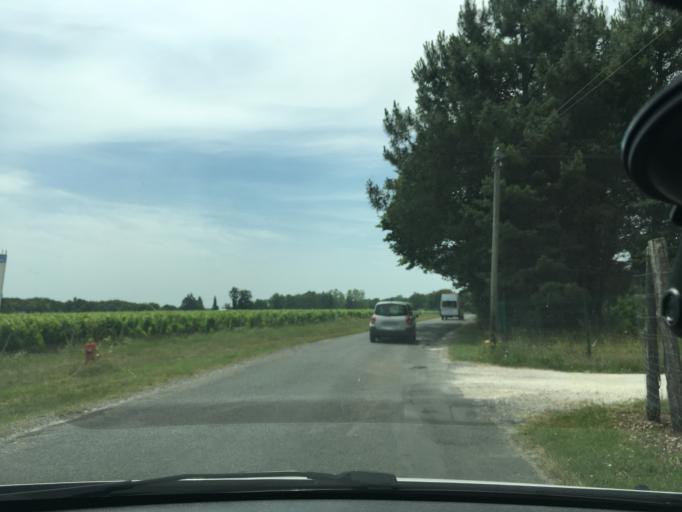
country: FR
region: Aquitaine
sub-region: Departement de la Gironde
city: Castelnau-de-Medoc
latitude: 45.0411
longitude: -0.8036
